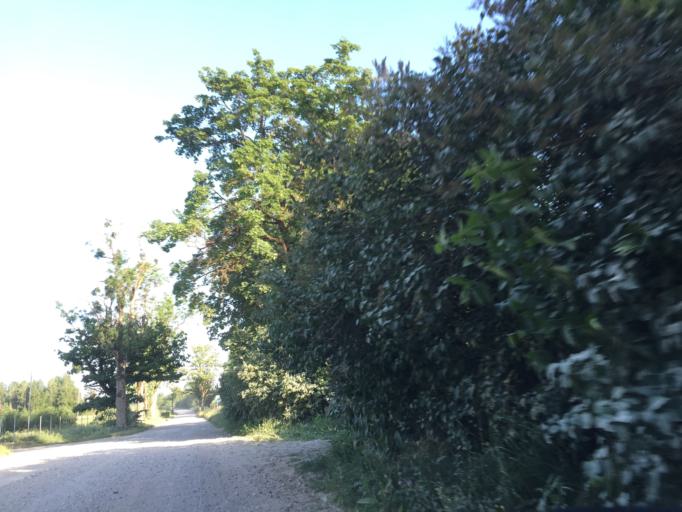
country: LV
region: Skriveri
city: Skriveri
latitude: 56.8361
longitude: 25.2128
